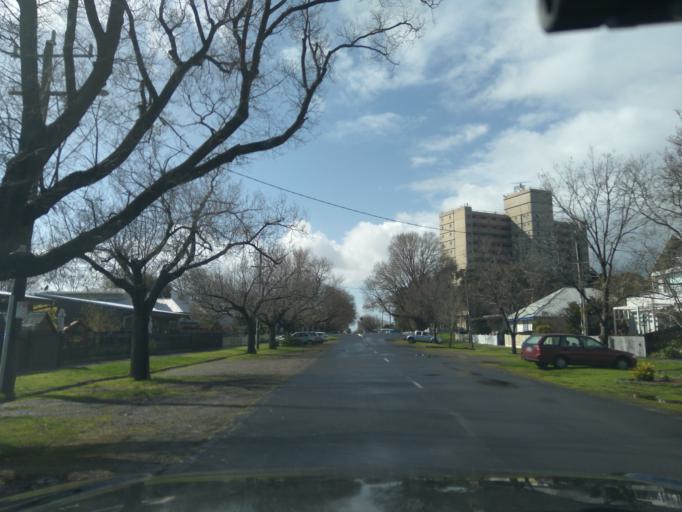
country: AU
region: Victoria
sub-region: Hobsons Bay
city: Williamstown
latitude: -37.8659
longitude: 144.9026
